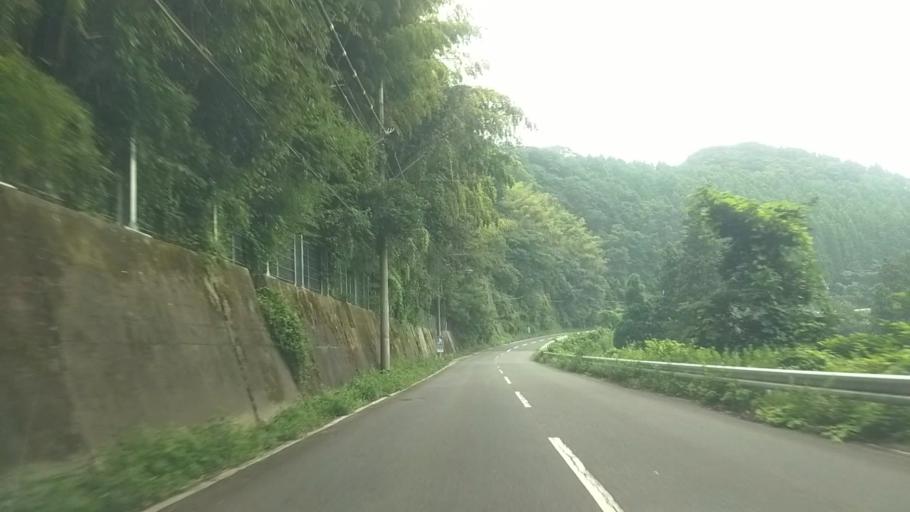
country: JP
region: Chiba
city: Katsuura
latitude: 35.2446
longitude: 140.2417
